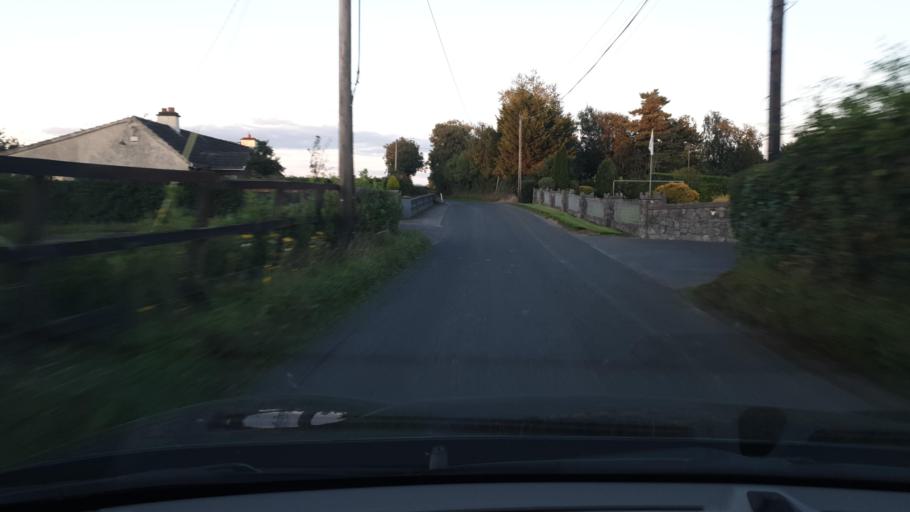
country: IE
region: Leinster
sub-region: Kildare
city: Prosperous
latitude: 53.3233
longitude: -6.7970
